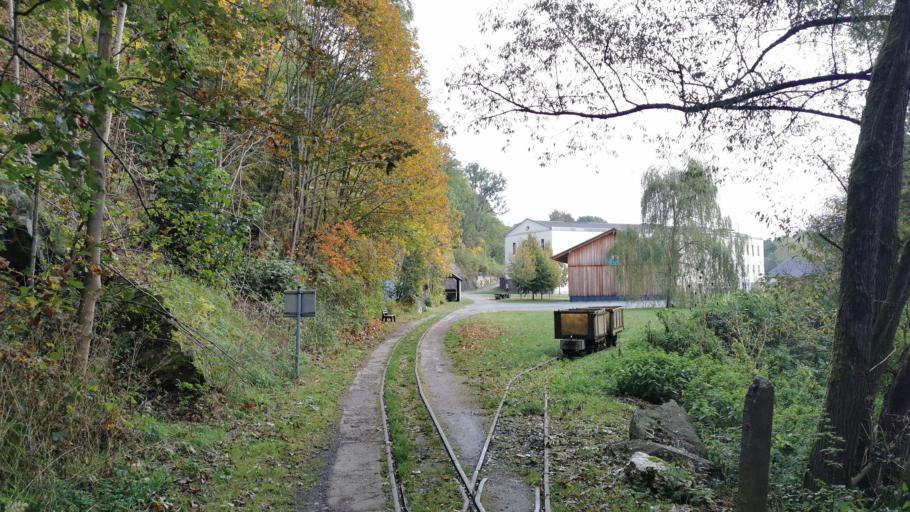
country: DE
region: Thuringia
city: Blankenberg
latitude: 50.3995
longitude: 11.7167
